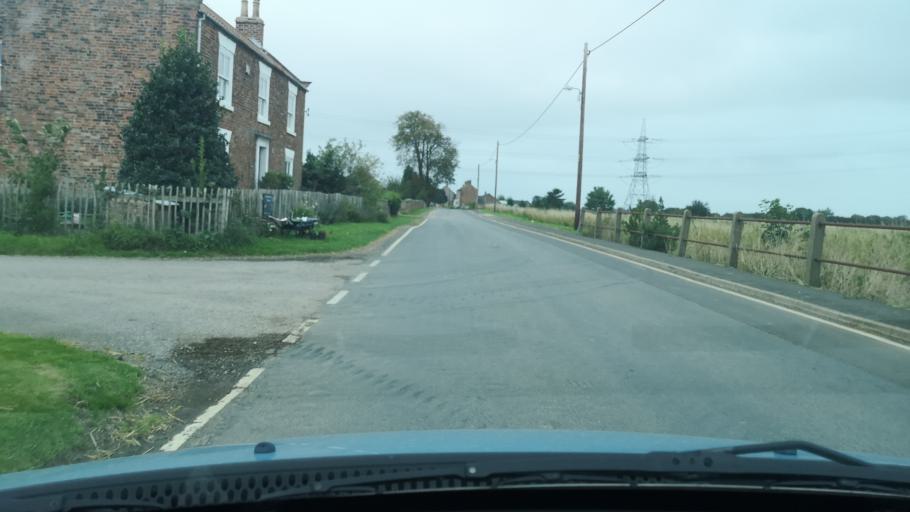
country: GB
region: England
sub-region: East Riding of Yorkshire
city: Laxton
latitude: 53.6983
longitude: -0.7410
